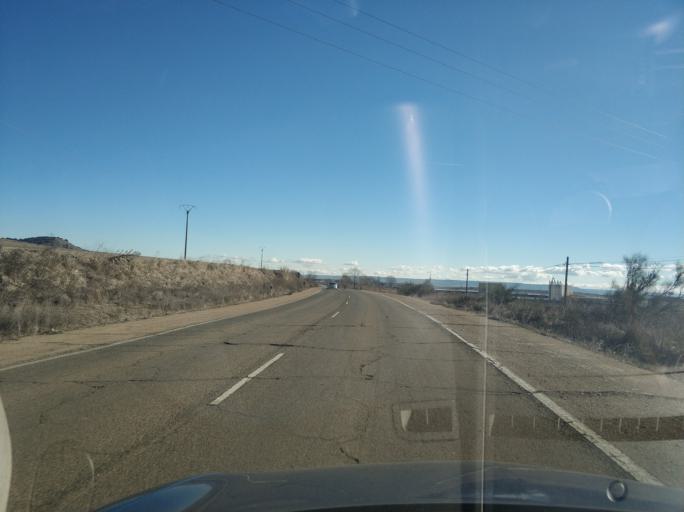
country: ES
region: Castille and Leon
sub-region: Provincia de Valladolid
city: Cisterniga
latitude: 41.6015
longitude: -4.6710
